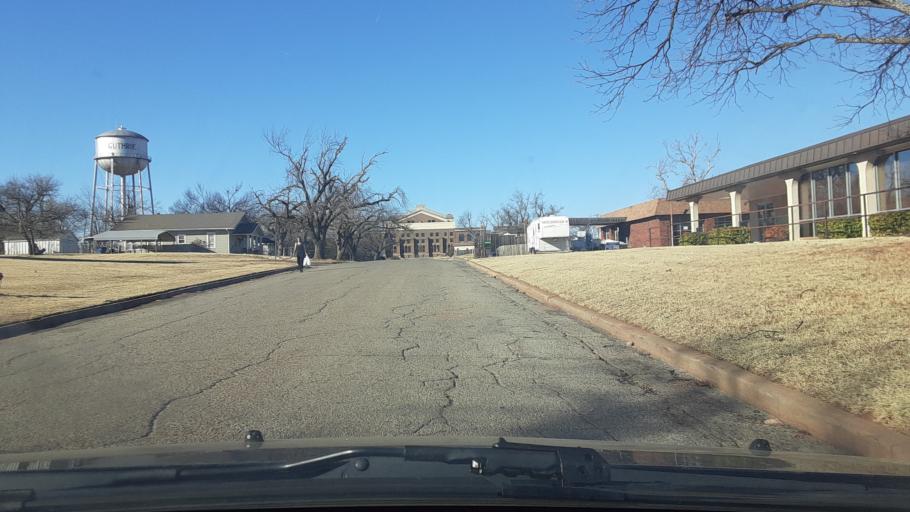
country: US
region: Oklahoma
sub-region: Logan County
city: Guthrie
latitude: 35.8781
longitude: -97.4093
